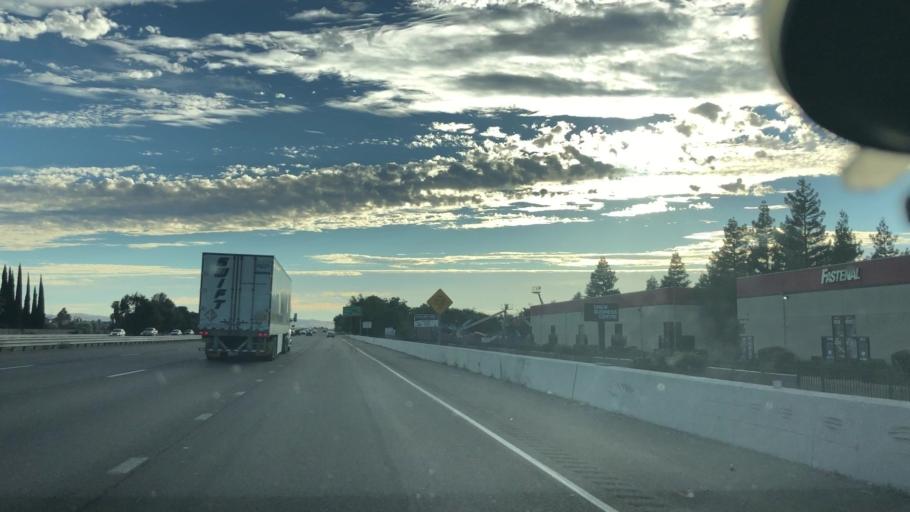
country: US
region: California
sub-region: San Joaquin County
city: Tracy
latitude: 37.7631
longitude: -121.4277
